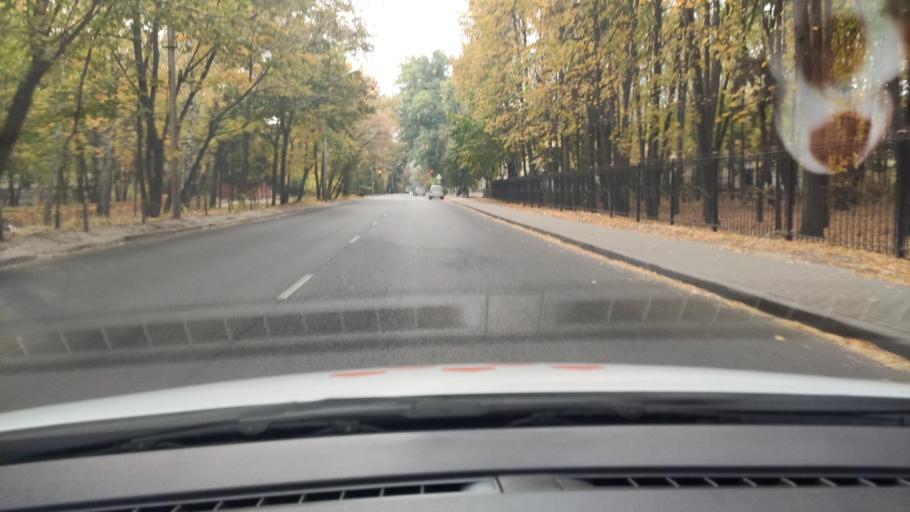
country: RU
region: Voronezj
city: Voronezh
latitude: 51.7174
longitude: 39.2214
